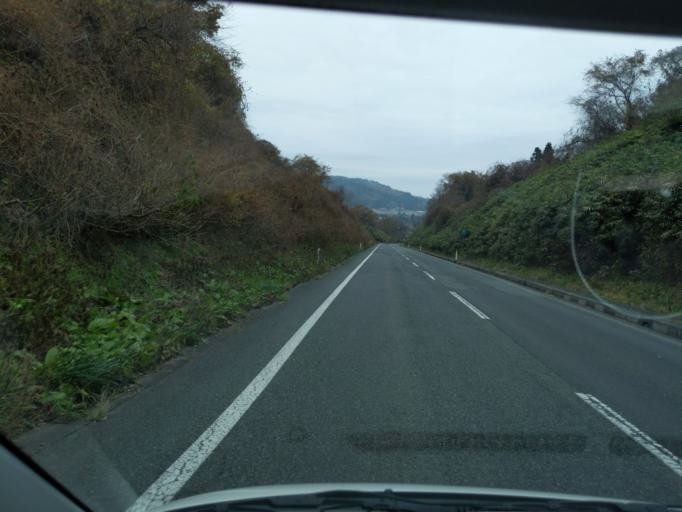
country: JP
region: Iwate
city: Mizusawa
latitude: 39.2084
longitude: 141.2199
